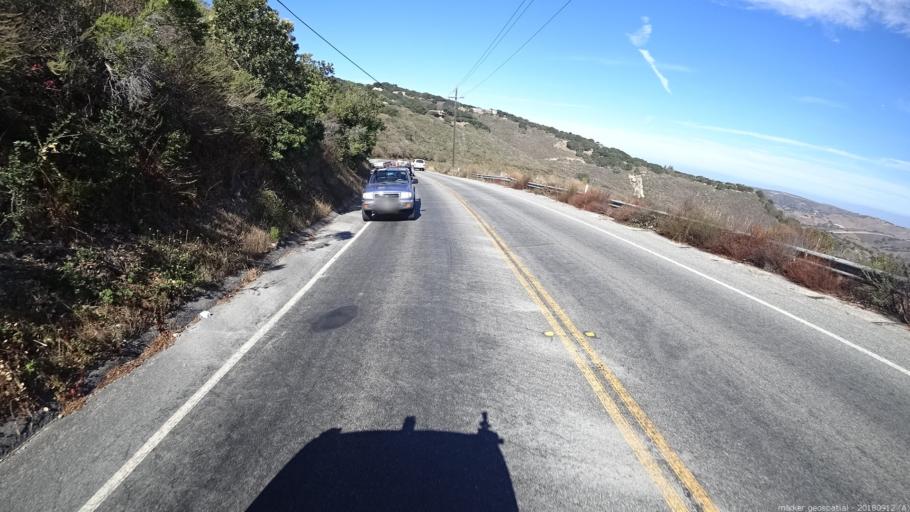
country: US
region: California
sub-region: Monterey County
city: Carmel Valley Village
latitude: 36.5524
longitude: -121.7551
